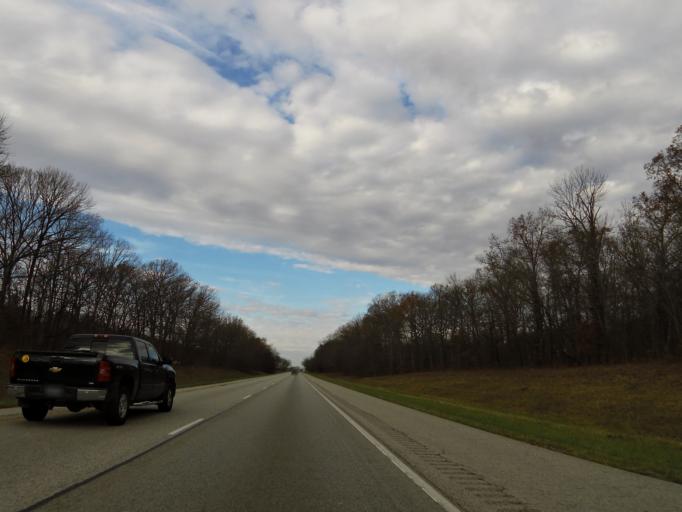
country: US
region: Illinois
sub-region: Washington County
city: Nashville
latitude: 38.4099
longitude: -89.4209
